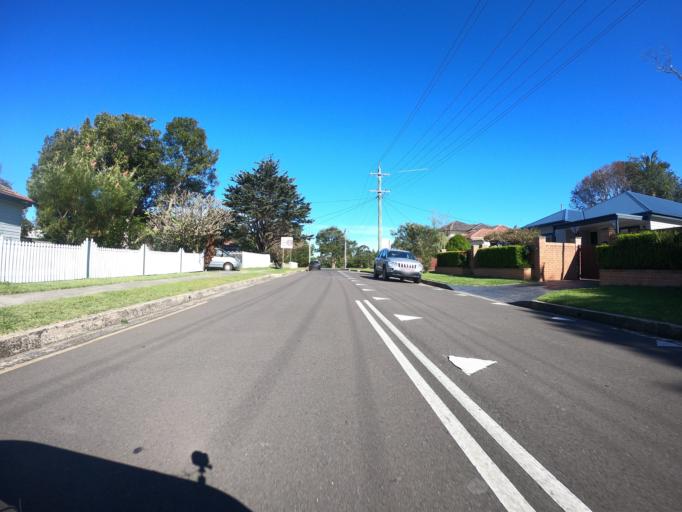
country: AU
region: New South Wales
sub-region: Wollongong
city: Corrimal
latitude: -34.3790
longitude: 150.9045
